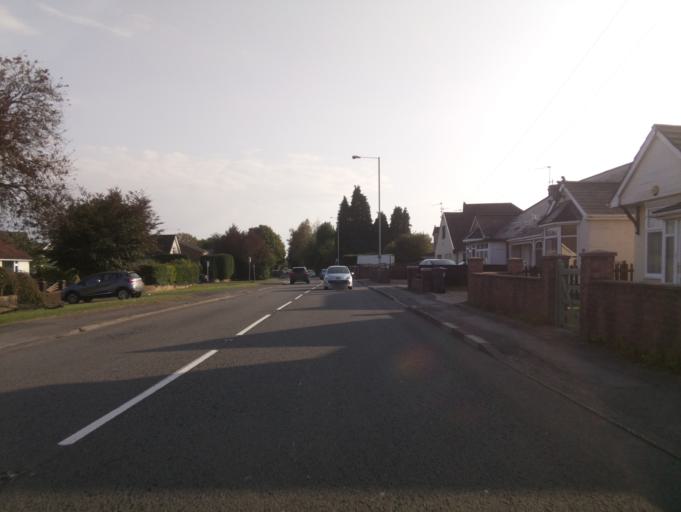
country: GB
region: Wales
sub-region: Torfaen County Borough
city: Cwmbran
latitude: 51.6681
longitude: -3.0178
